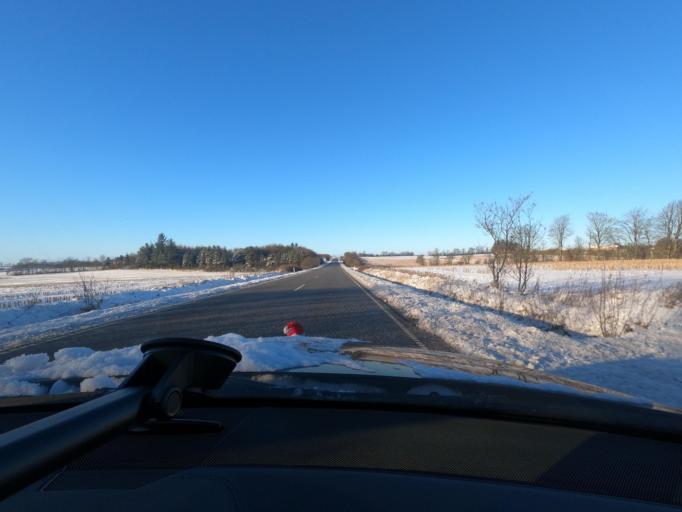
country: DK
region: South Denmark
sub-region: Tonder Kommune
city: Toftlund
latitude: 55.1164
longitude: 9.1633
